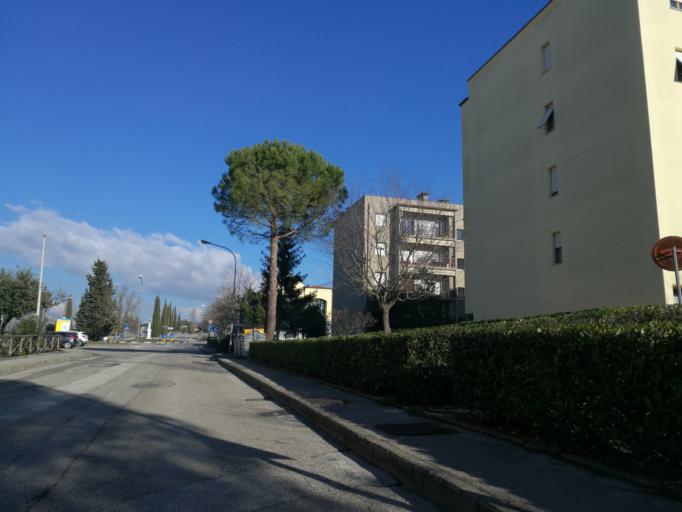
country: IT
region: Umbria
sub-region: Provincia di Perugia
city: Perugia
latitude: 43.0806
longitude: 12.3685
